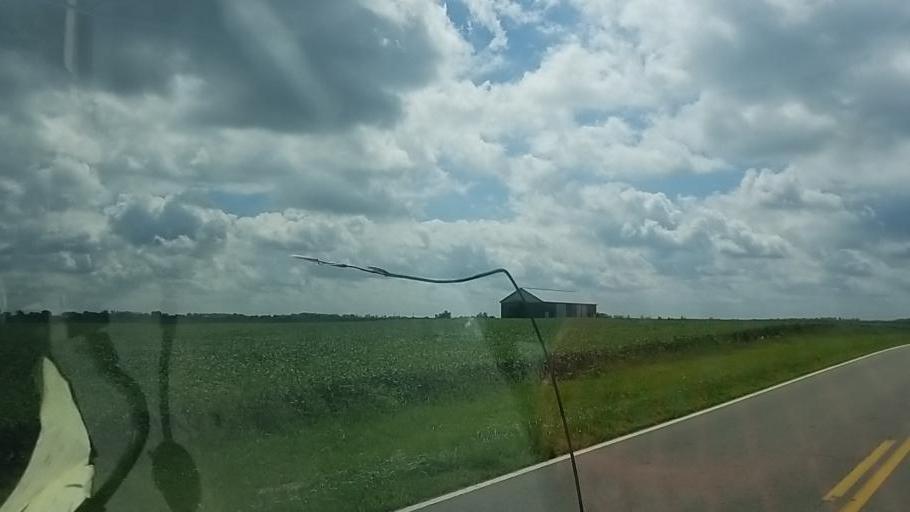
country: US
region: Ohio
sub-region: Fayette County
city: Jeffersonville
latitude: 39.6833
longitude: -83.5038
